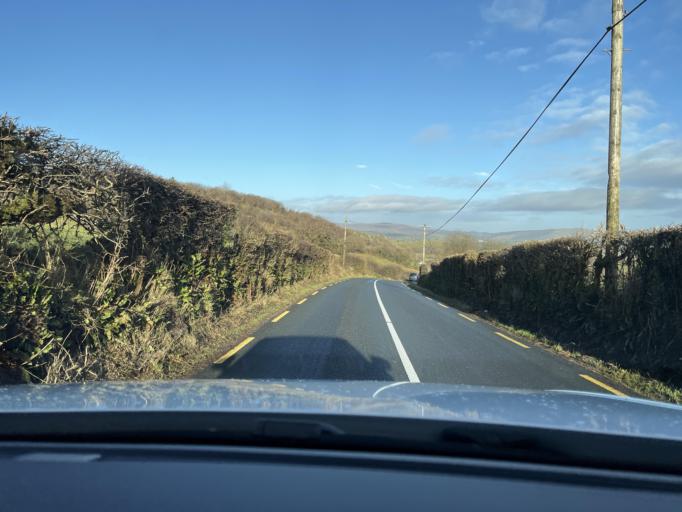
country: IE
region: Connaught
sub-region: County Leitrim
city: Manorhamilton
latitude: 54.2843
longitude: -8.2631
